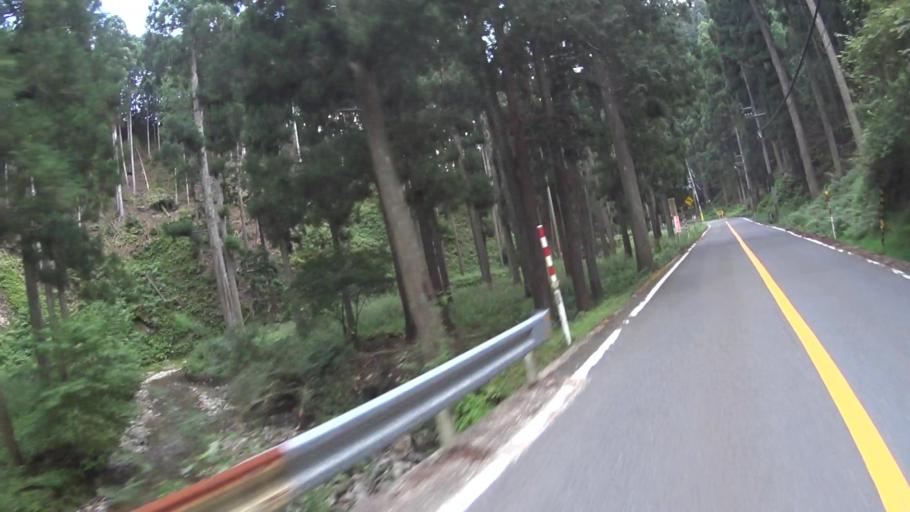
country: JP
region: Kyoto
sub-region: Kyoto-shi
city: Kamigyo-ku
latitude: 35.2427
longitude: 135.6528
